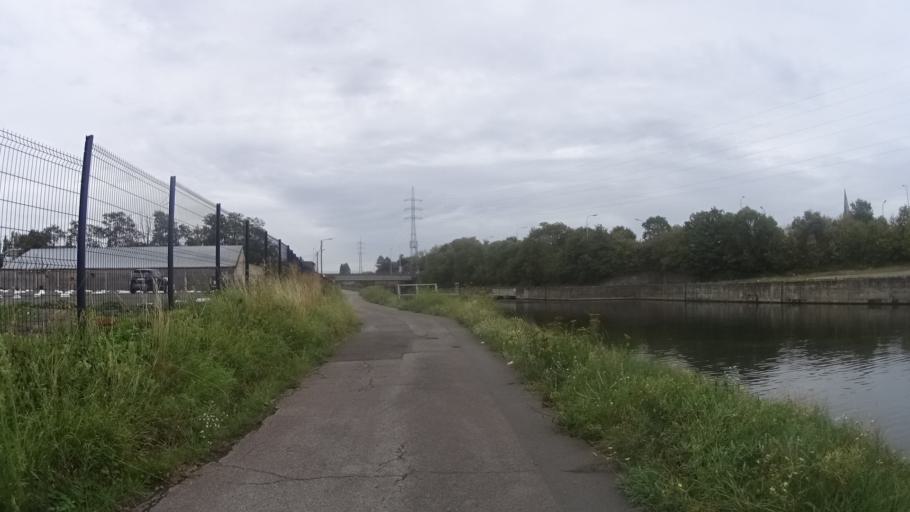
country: BE
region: Wallonia
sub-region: Province du Hainaut
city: Chatelet
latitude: 50.4060
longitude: 4.5161
